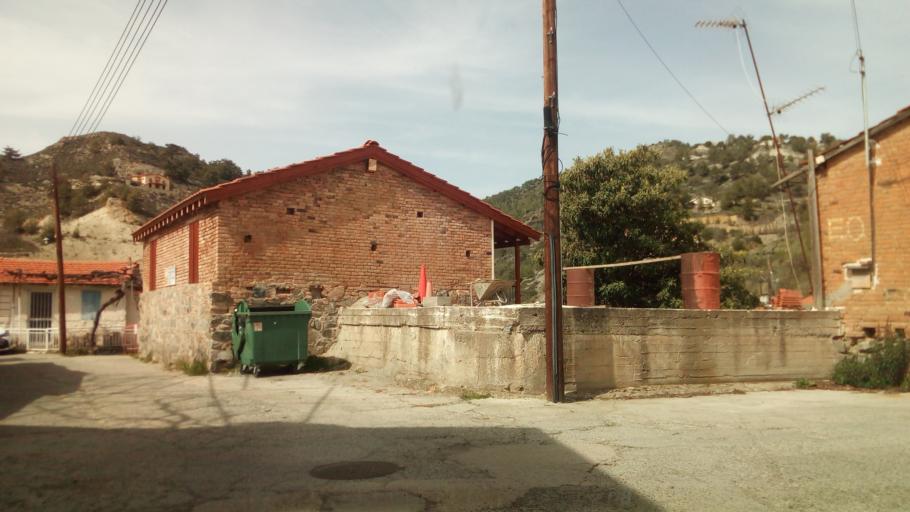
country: CY
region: Limassol
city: Pelendri
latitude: 34.8950
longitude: 32.9640
